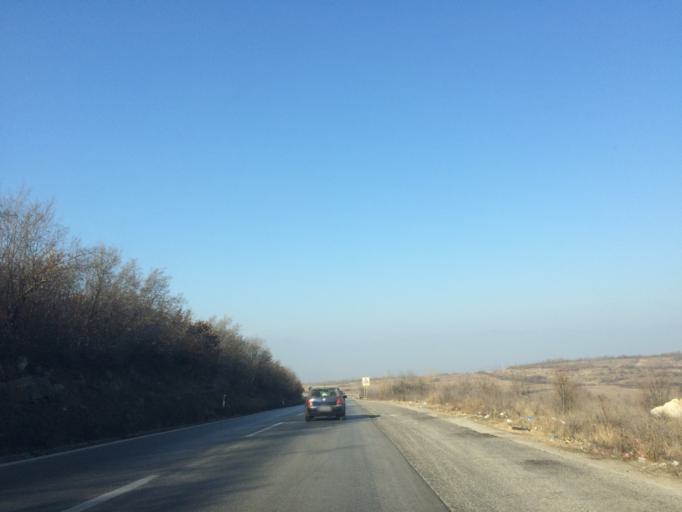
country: XK
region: Pec
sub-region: Komuna e Klines
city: Klina
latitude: 42.5957
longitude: 20.6106
